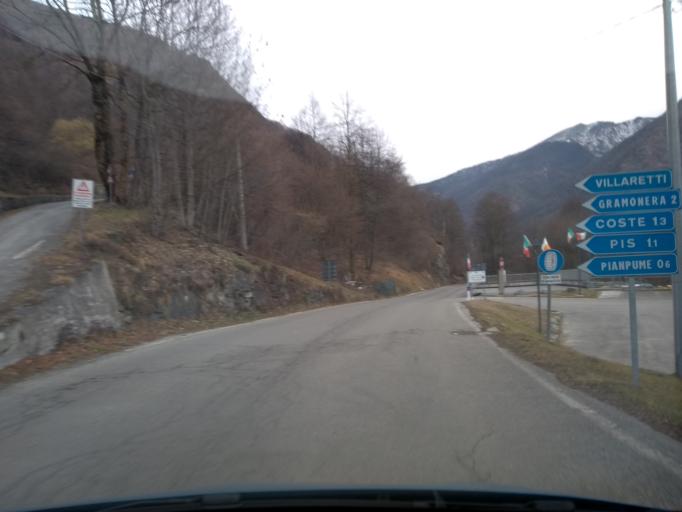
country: IT
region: Piedmont
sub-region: Provincia di Torino
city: Lemie
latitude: 45.2288
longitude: 7.2951
